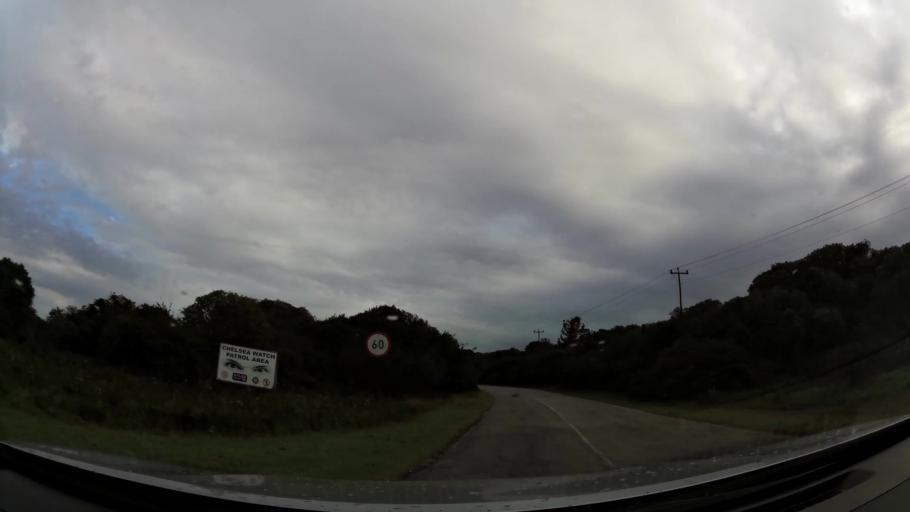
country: ZA
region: Eastern Cape
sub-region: Nelson Mandela Bay Metropolitan Municipality
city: Port Elizabeth
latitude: -34.0108
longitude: 25.4959
